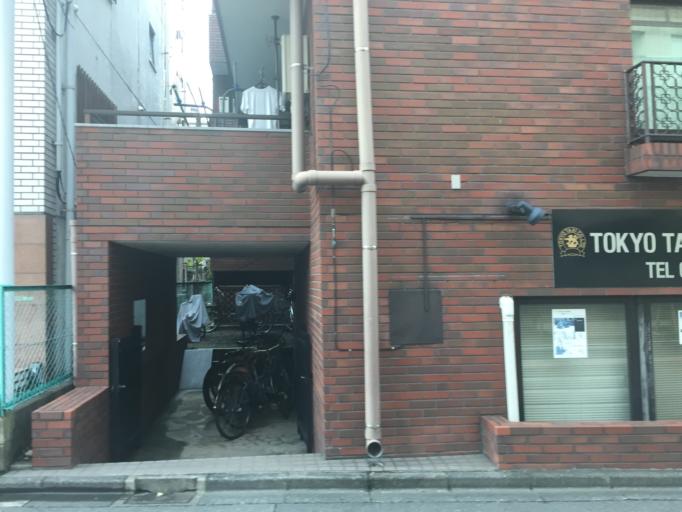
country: JP
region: Tokyo
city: Tokyo
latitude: 35.6167
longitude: 139.6501
